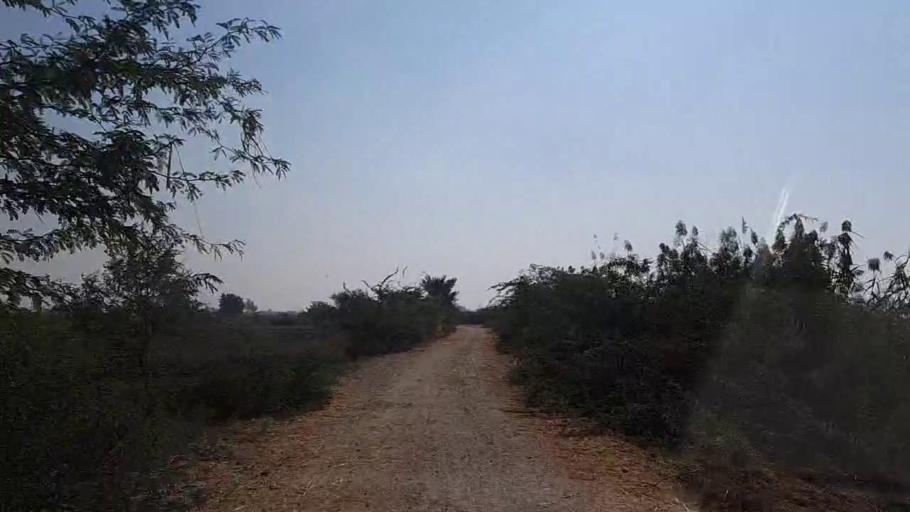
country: PK
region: Sindh
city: Thatta
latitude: 24.7952
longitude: 67.9689
